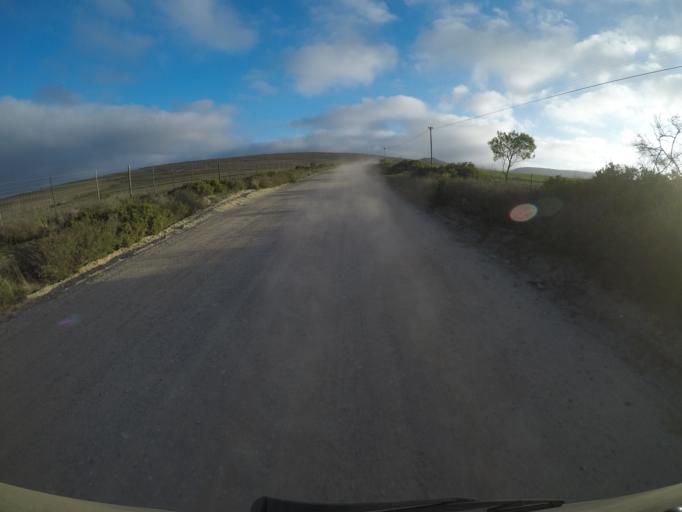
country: ZA
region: Western Cape
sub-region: Eden District Municipality
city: Mossel Bay
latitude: -34.1232
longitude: 22.0532
